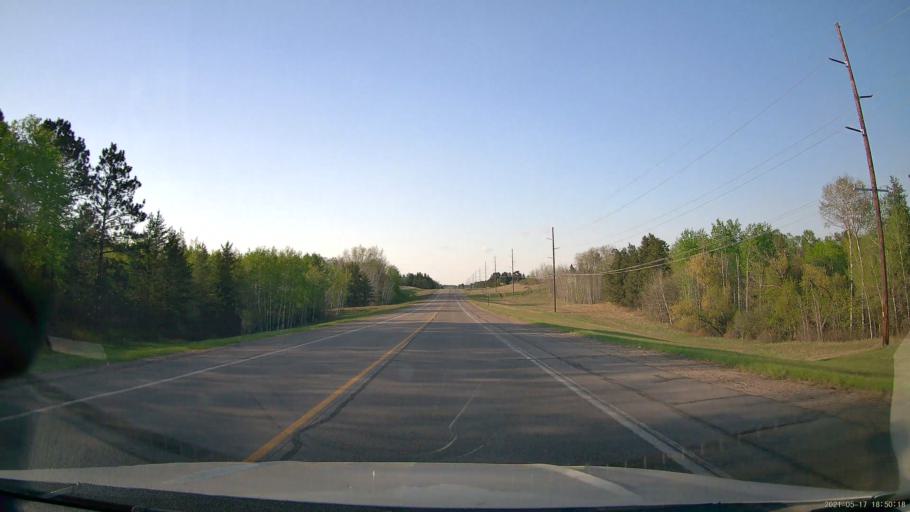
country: US
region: Minnesota
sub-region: Hubbard County
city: Park Rapids
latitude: 46.9323
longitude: -95.0168
